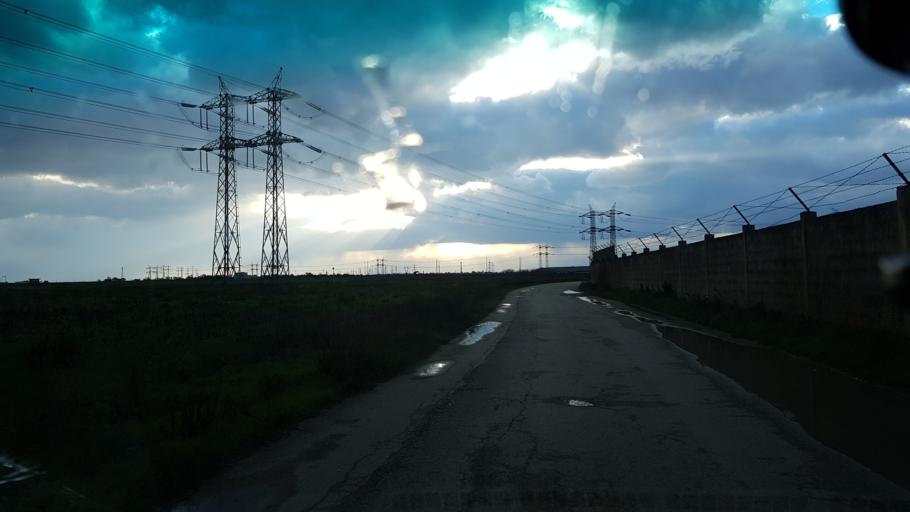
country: IT
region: Apulia
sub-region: Provincia di Brindisi
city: La Rosa
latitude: 40.6240
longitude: 17.9952
